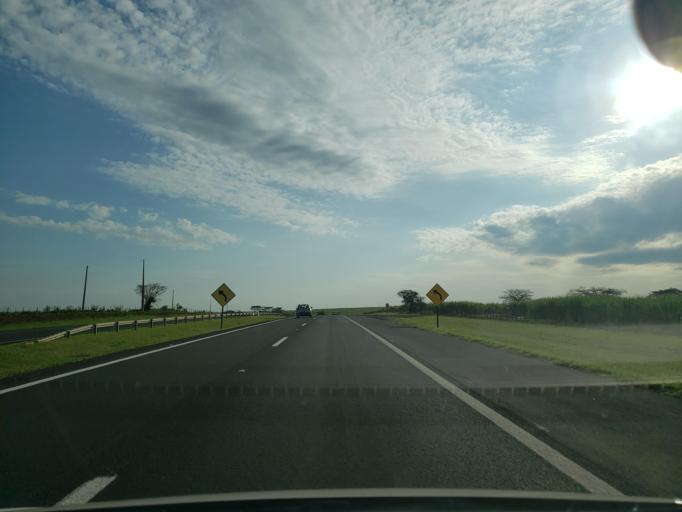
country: BR
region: Sao Paulo
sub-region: Valparaiso
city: Valparaiso
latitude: -21.2044
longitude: -50.8032
